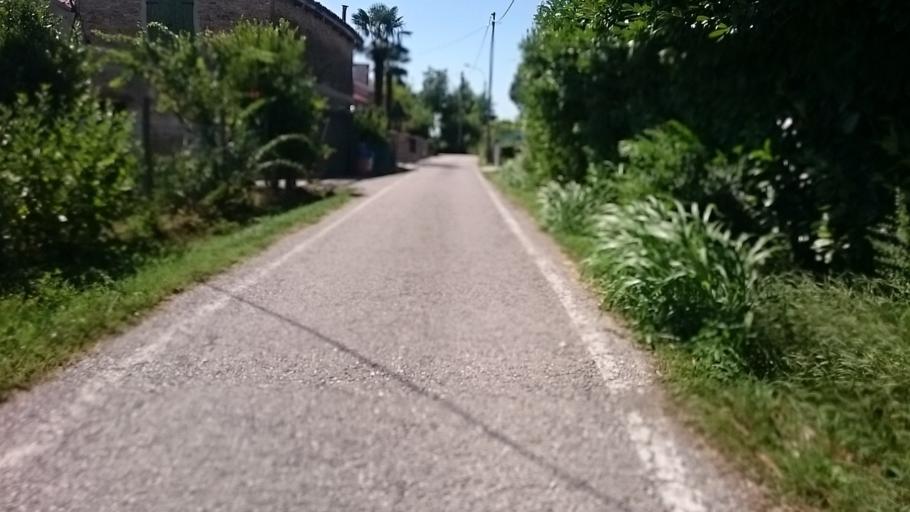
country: IT
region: Veneto
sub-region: Provincia di Venezia
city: Fiesso d'Artico
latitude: 45.4382
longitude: 12.0245
